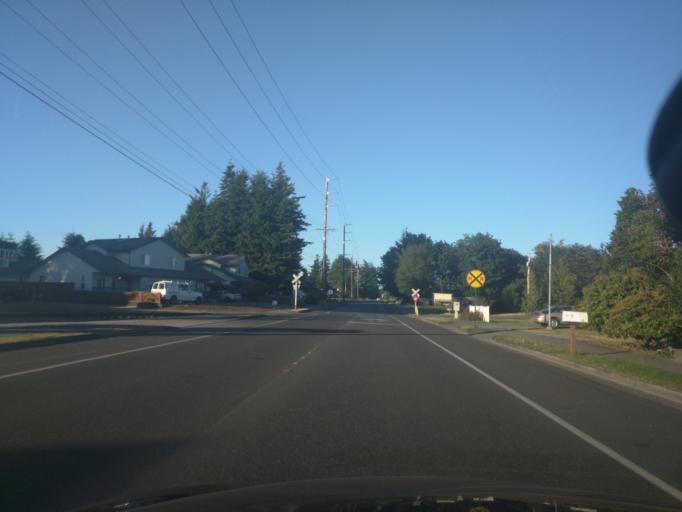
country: US
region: Washington
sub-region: Whatcom County
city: Lynden
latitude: 48.9493
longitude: -122.4351
